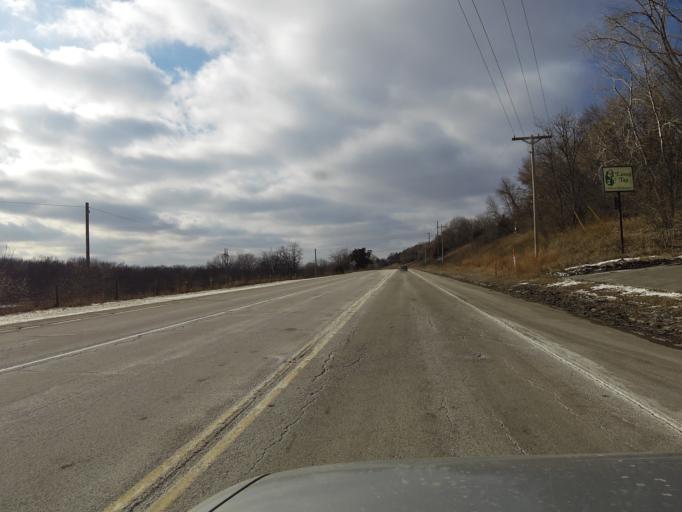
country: US
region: Minnesota
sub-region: Hennepin County
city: Eden Prairie
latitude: 44.8182
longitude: -93.4825
